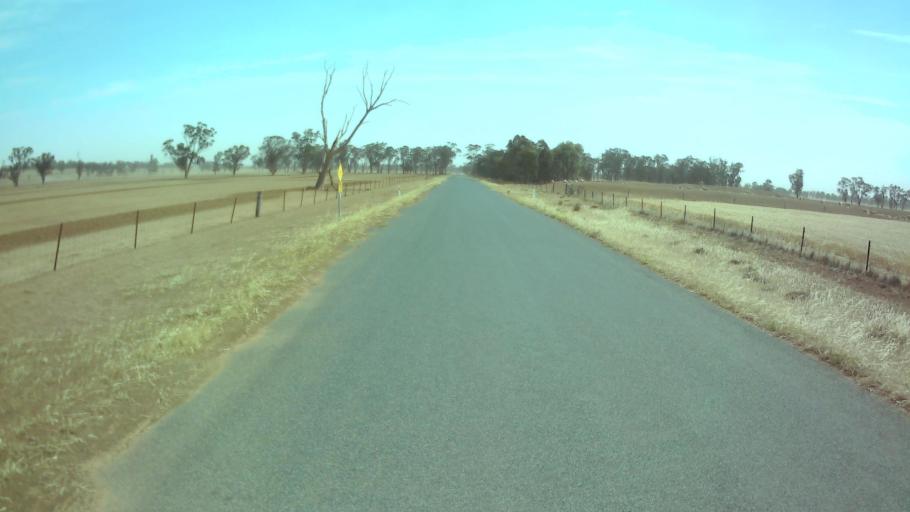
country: AU
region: New South Wales
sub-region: Weddin
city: Grenfell
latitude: -33.7203
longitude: 147.9999
